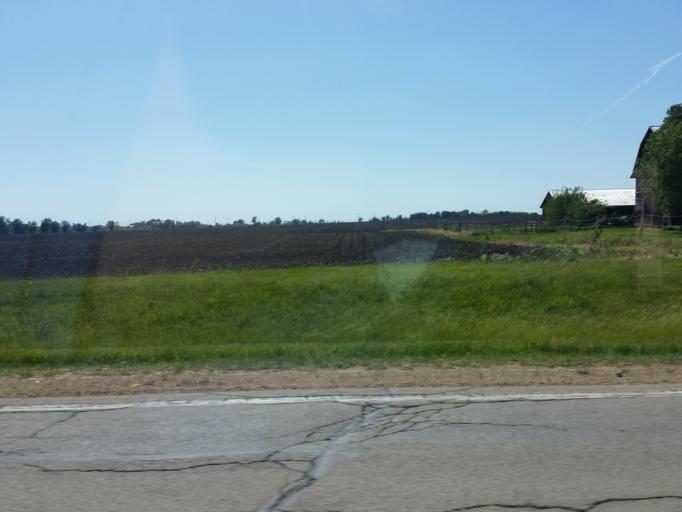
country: US
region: Illinois
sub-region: Ogle County
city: Davis Junction
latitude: 42.1128
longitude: -89.0764
